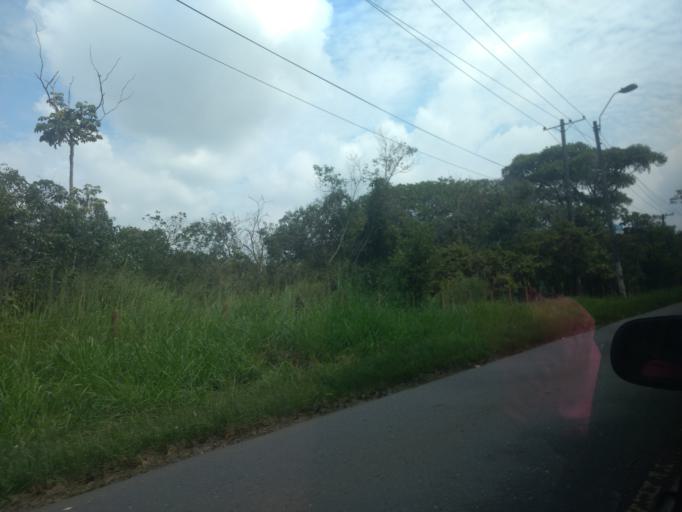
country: CO
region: Valle del Cauca
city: Cali
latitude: 3.3624
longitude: -76.5509
